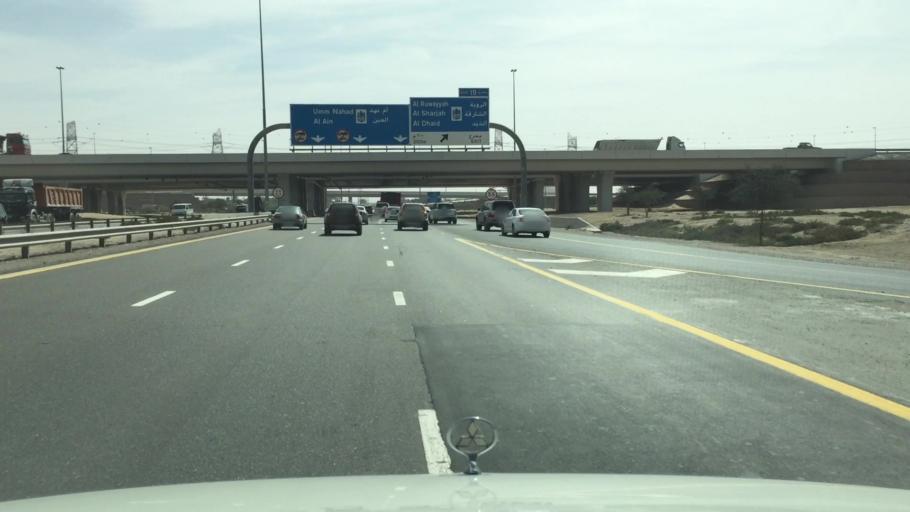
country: AE
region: Dubai
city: Dubai
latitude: 25.0884
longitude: 55.3911
